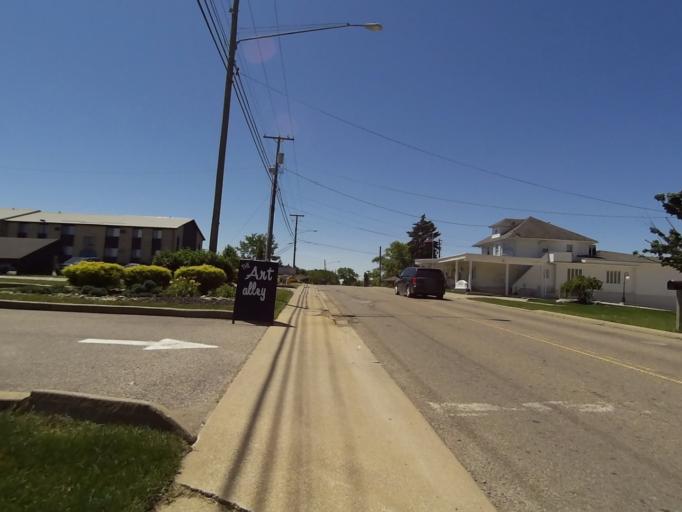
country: US
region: Ohio
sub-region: Jefferson County
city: Wintersville
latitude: 40.3722
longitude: -80.6985
